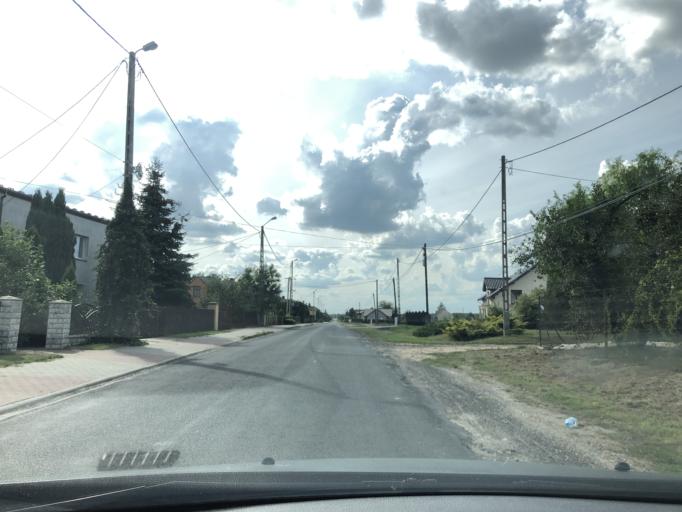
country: PL
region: Lodz Voivodeship
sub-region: Powiat wieruszowski
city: Walichnowy
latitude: 51.2616
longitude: 18.3921
